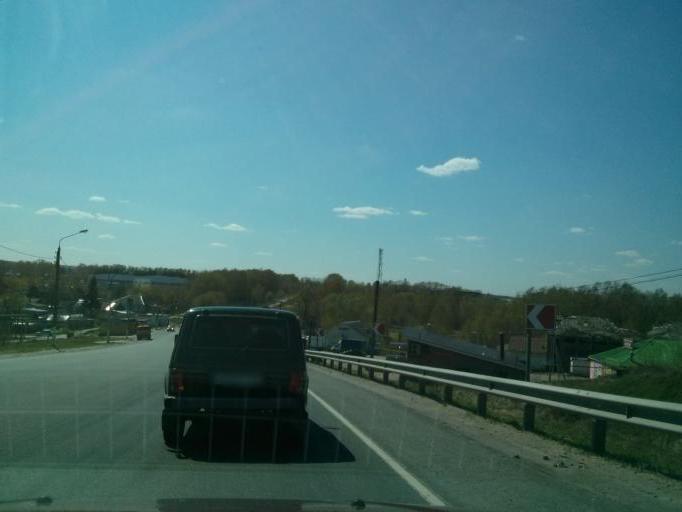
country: RU
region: Nizjnij Novgorod
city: Burevestnik
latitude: 56.1768
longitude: 43.7708
